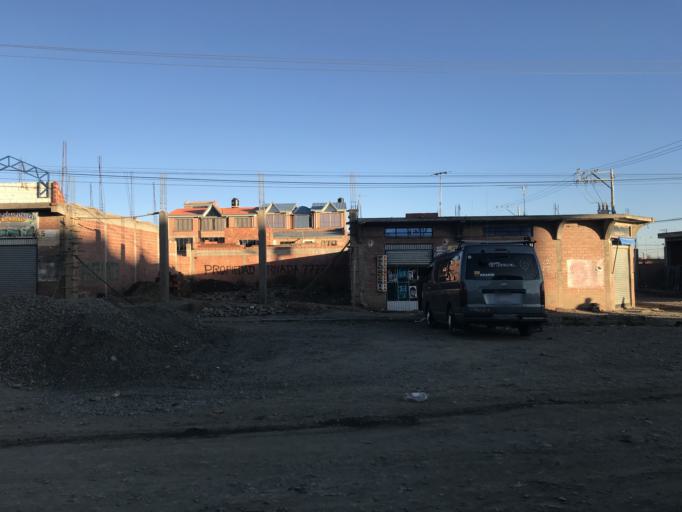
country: BO
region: La Paz
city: La Paz
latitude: -16.5045
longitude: -68.2502
